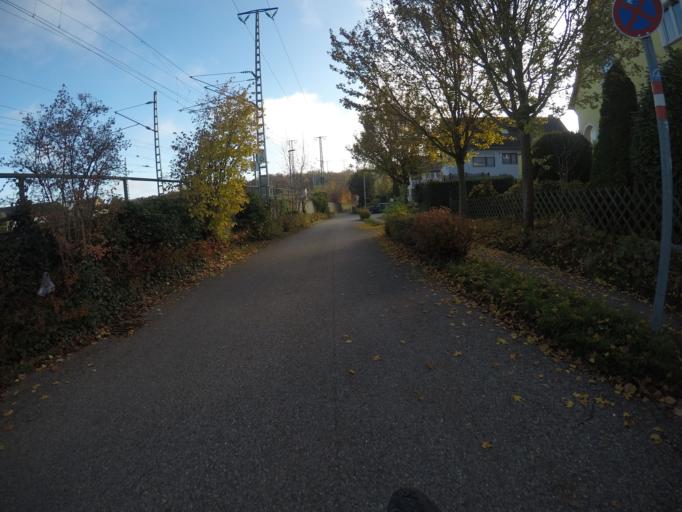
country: DE
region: Baden-Wuerttemberg
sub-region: Regierungsbezirk Stuttgart
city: Steinenbronn
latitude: 48.7161
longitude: 9.1095
